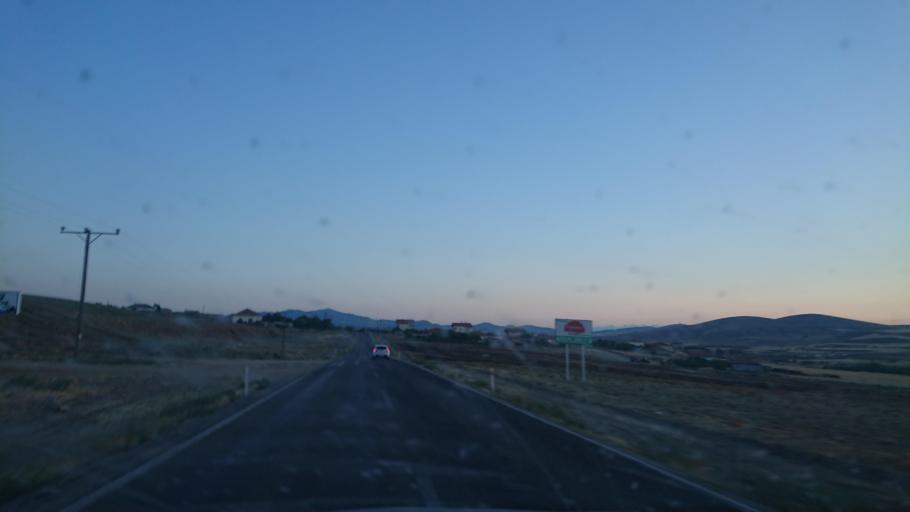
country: TR
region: Aksaray
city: Balci
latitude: 38.7985
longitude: 34.1282
